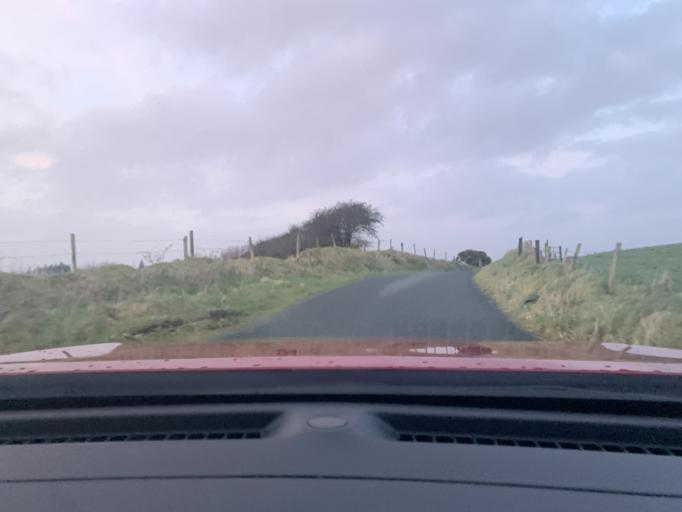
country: IE
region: Connaught
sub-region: Sligo
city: Ballymote
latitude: 54.0648
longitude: -8.3994
